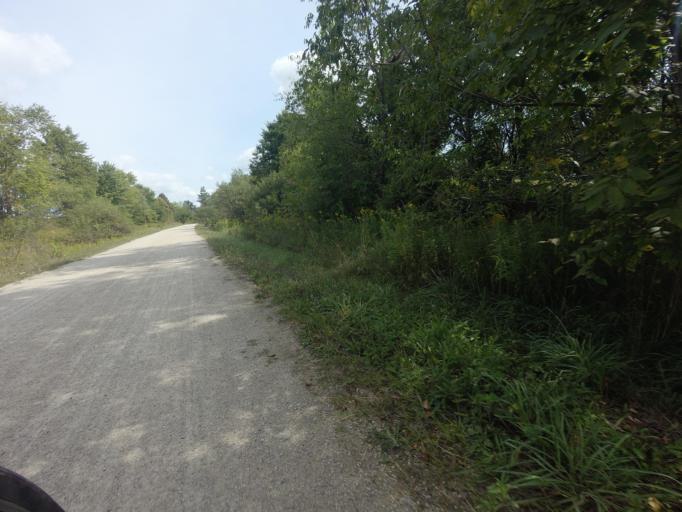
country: CA
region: Ontario
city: Waterloo
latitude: 43.6128
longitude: -80.5731
